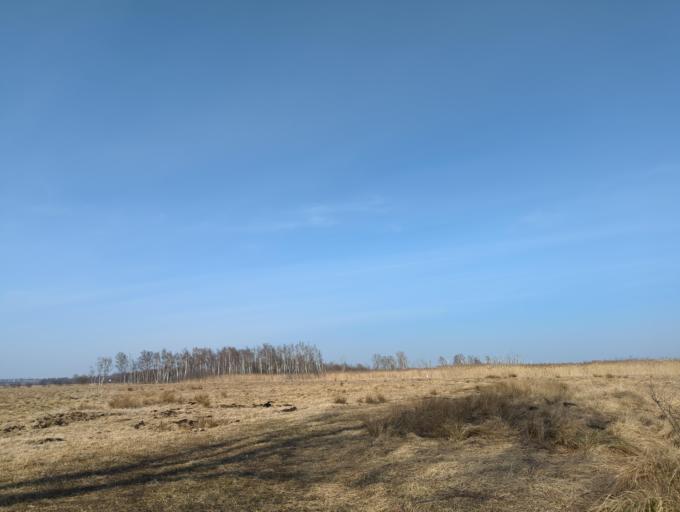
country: DE
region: Bavaria
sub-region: Swabia
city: Leipheim
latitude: 48.4847
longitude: 10.2141
